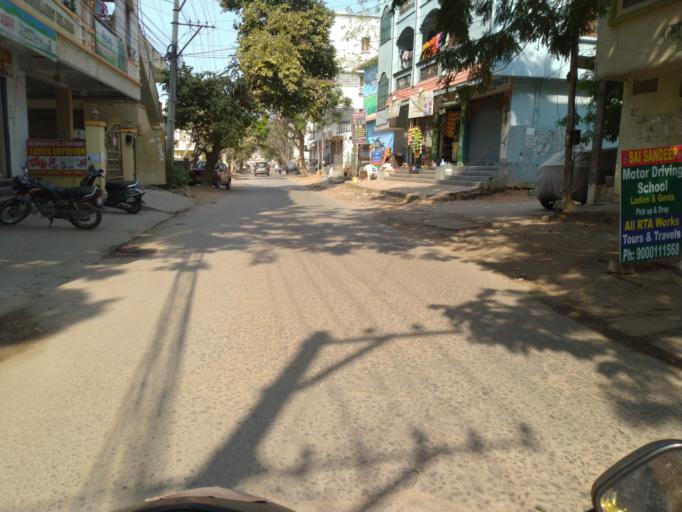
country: IN
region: Telangana
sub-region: Rangareddi
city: Quthbullapur
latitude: 17.4999
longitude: 78.4709
